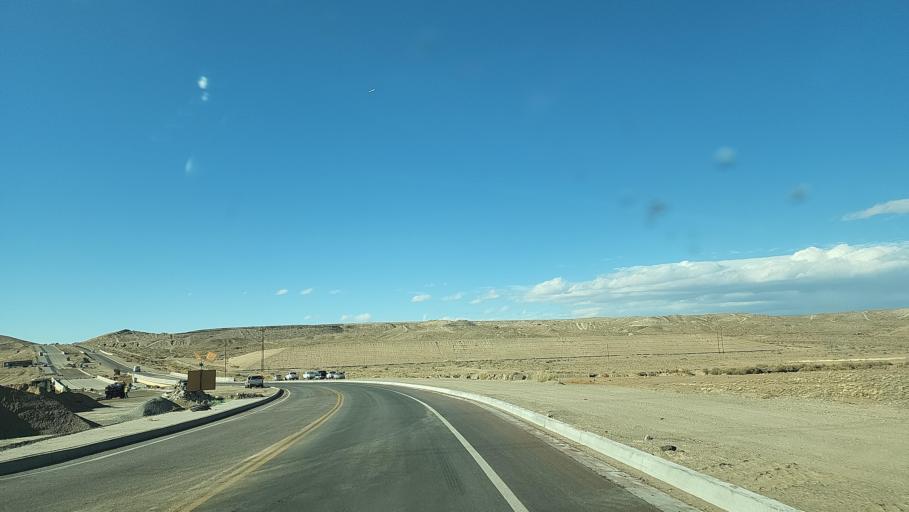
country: US
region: New Mexico
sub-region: Bernalillo County
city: South Valley
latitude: 35.0091
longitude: -106.6267
